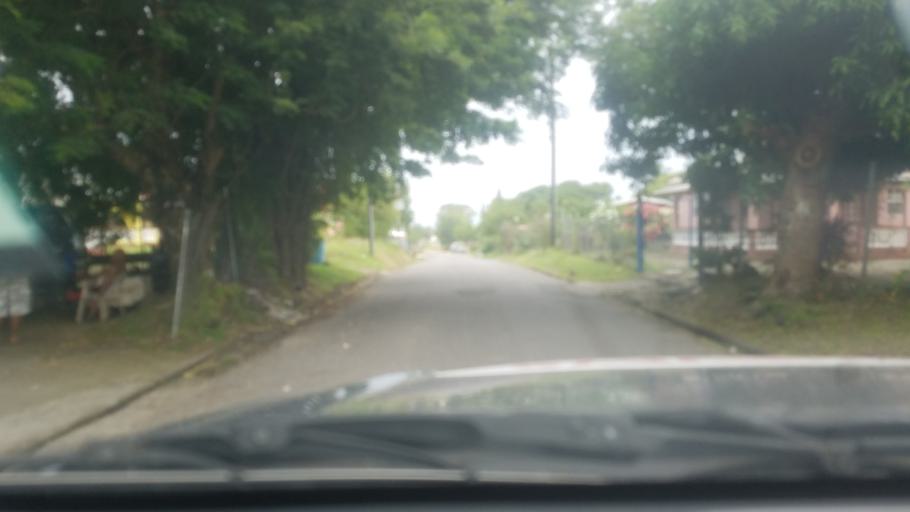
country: LC
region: Laborie Quarter
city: Laborie
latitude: 13.7562
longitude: -60.9803
